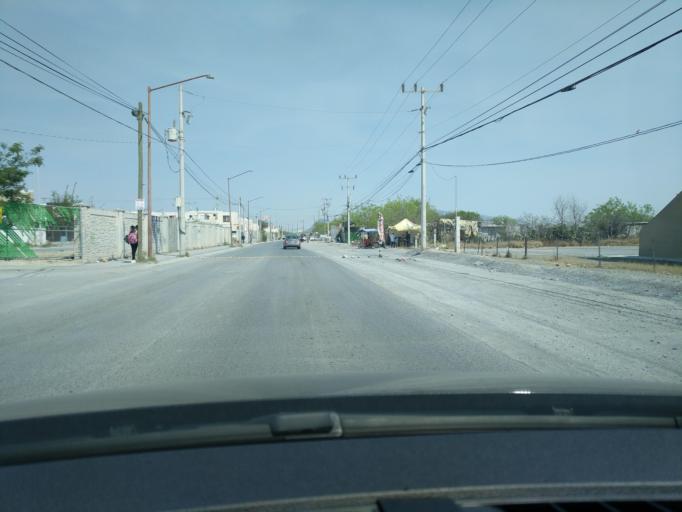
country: MX
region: Nuevo Leon
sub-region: Garcia
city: Valle de Lincoln
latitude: 25.7927
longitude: -100.4773
